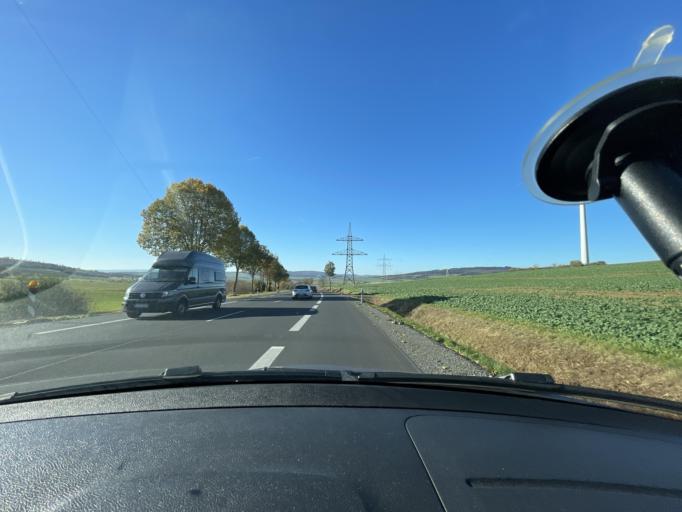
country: DE
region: Lower Saxony
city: Einbeck
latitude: 51.8661
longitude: 9.8891
